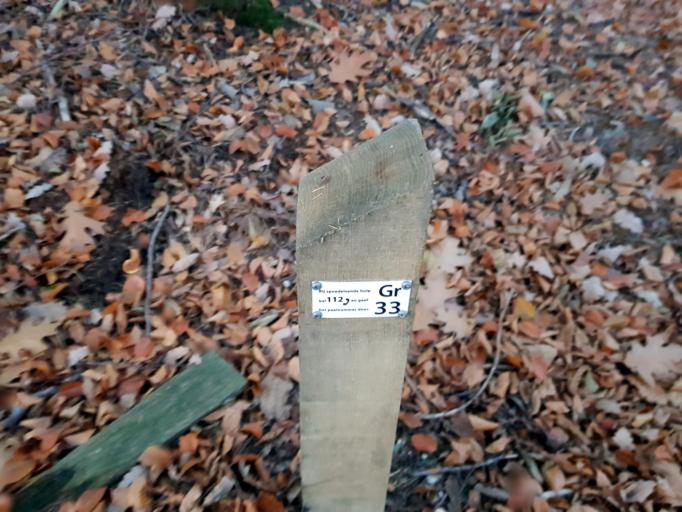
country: NL
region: Gelderland
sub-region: Gemeente Groesbeek
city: Groesbeek
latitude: 51.7772
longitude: 5.9084
